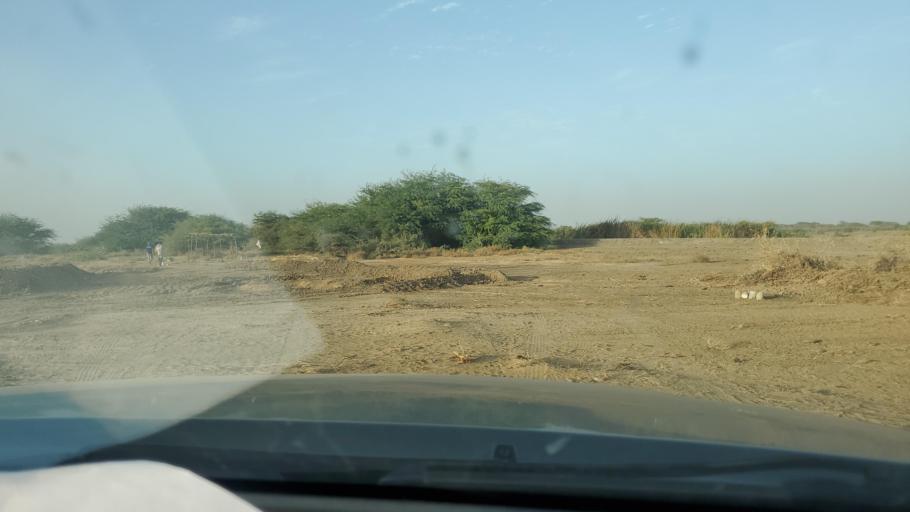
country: SN
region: Saint-Louis
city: Saint-Louis
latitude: 15.9394
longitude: -16.4167
